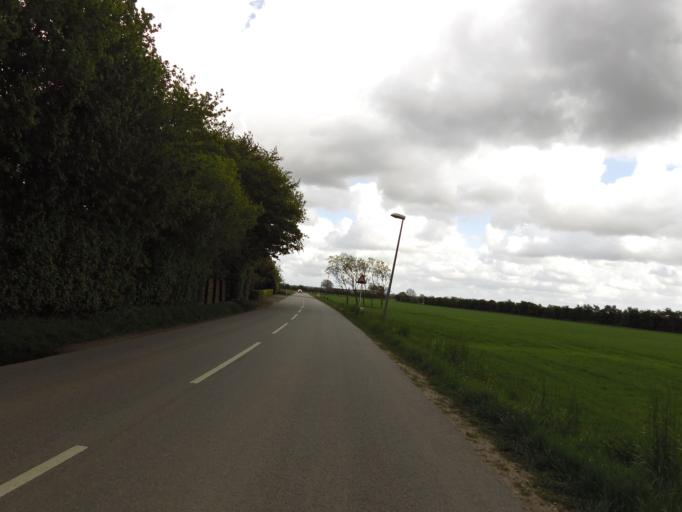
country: DK
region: South Denmark
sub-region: Haderslev Kommune
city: Gram
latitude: 55.3130
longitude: 8.9863
